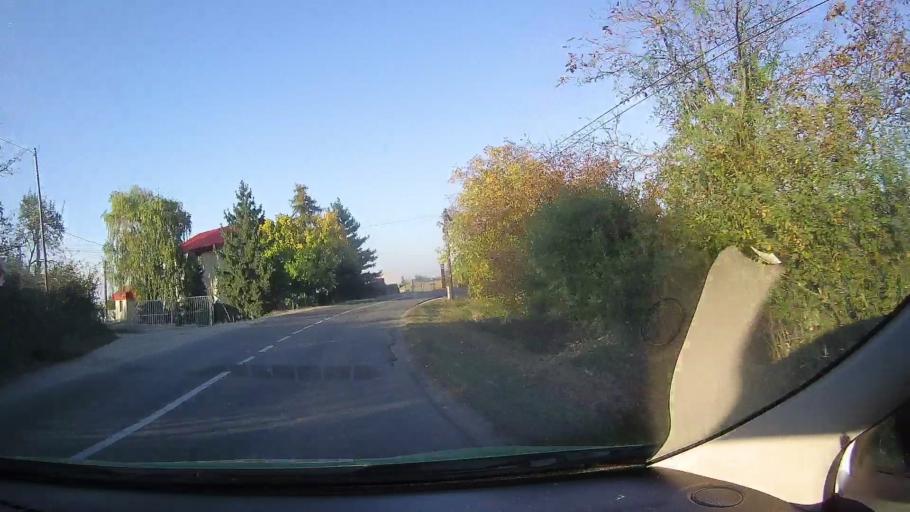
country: RO
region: Bihor
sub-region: Comuna Paleu
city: Paleu
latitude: 47.1082
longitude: 21.9283
